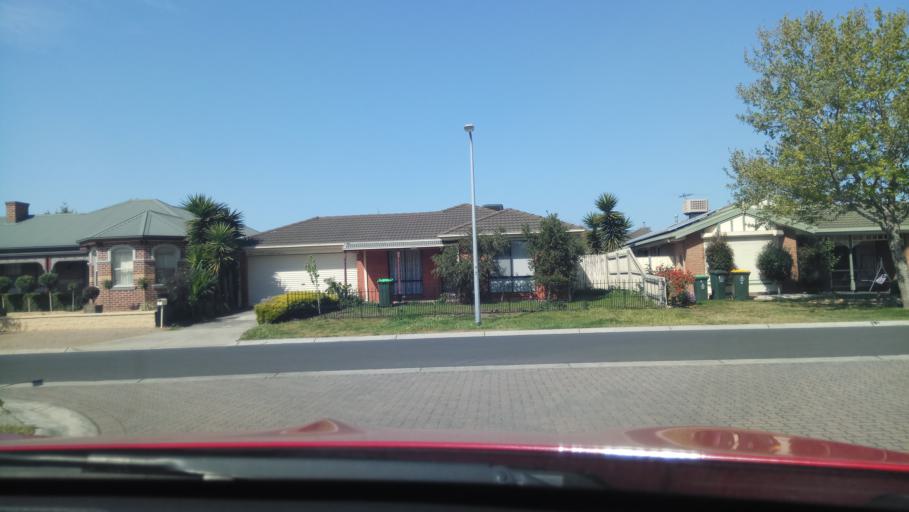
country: AU
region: Victoria
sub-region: Wyndham
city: Williams Landing
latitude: -37.8854
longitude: 144.7537
